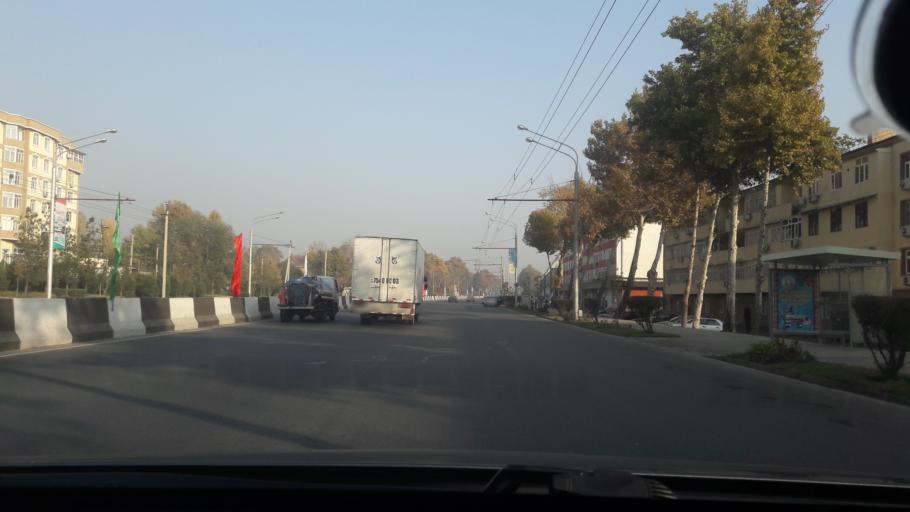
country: TJ
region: Dushanbe
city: Dushanbe
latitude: 38.5532
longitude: 68.8515
